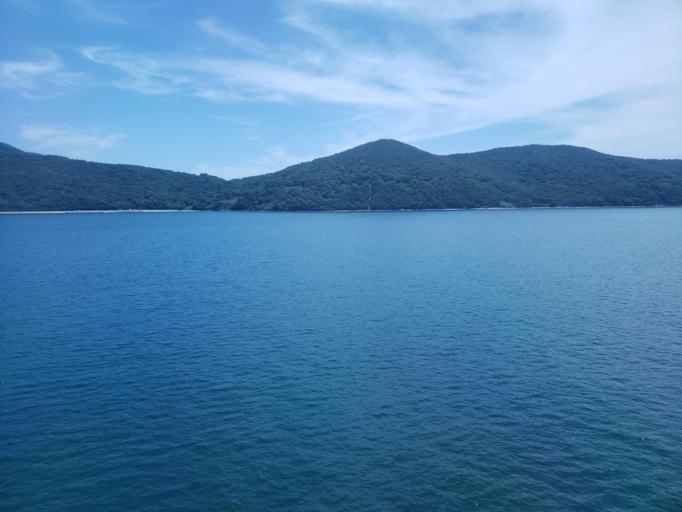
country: JP
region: Kagawa
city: Tonosho
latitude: 34.4398
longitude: 134.3180
